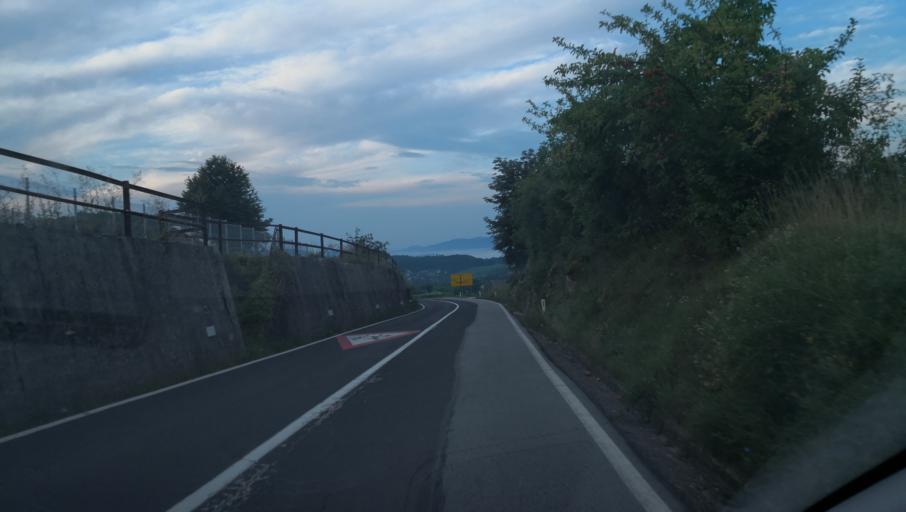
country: SI
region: Metlika
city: Metlika
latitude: 45.6833
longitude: 15.2805
